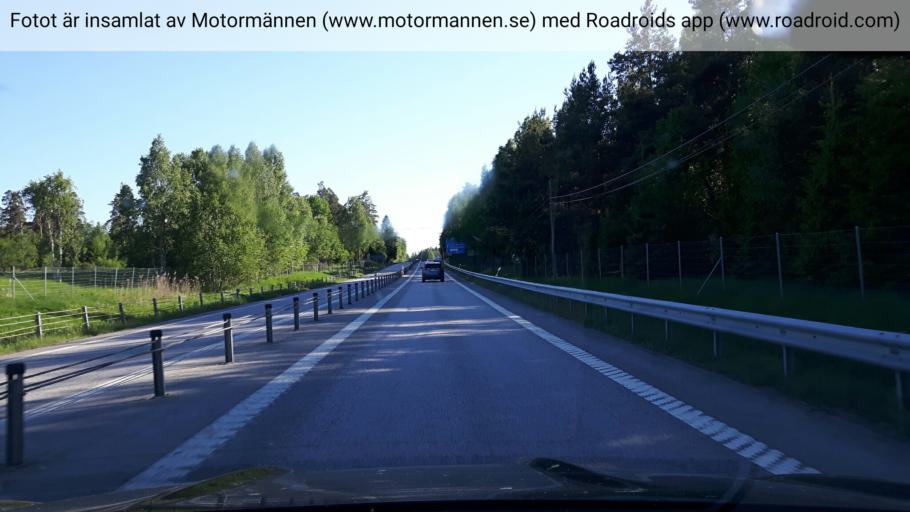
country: SE
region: Stockholm
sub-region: Vallentuna Kommun
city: Vallentuna
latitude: 59.5061
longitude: 18.1723
